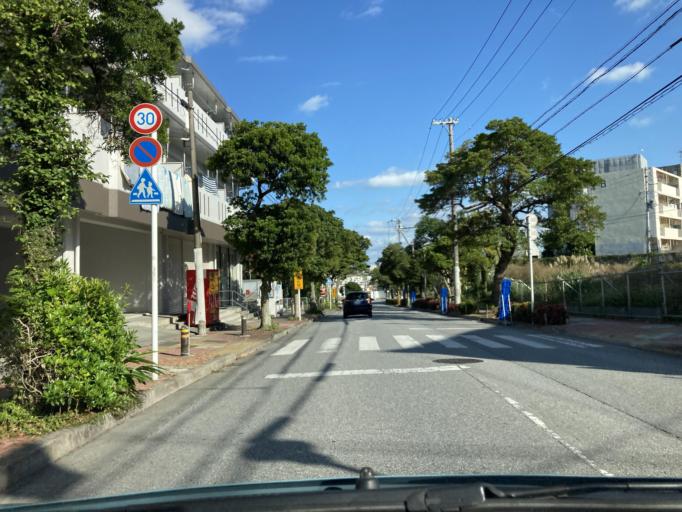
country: JP
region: Okinawa
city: Ginowan
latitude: 26.2267
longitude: 127.7325
